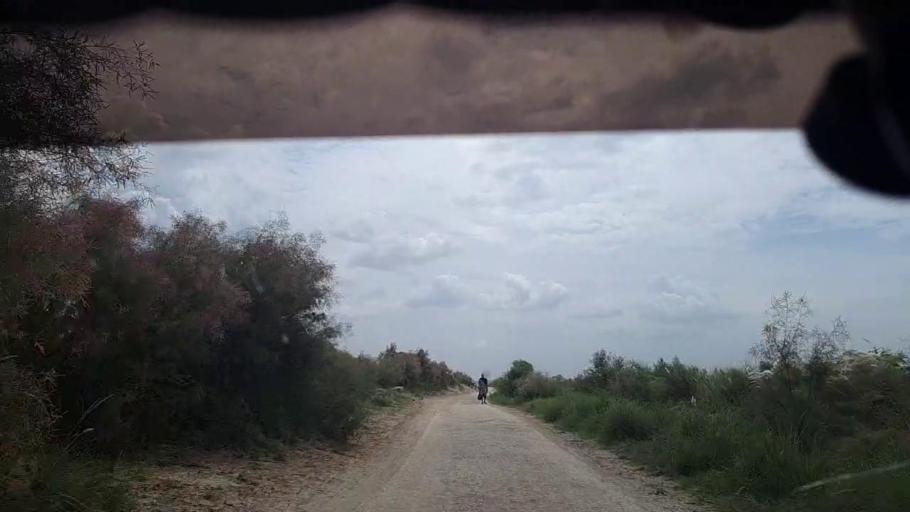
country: PK
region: Sindh
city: Rustam jo Goth
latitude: 28.0327
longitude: 68.9367
